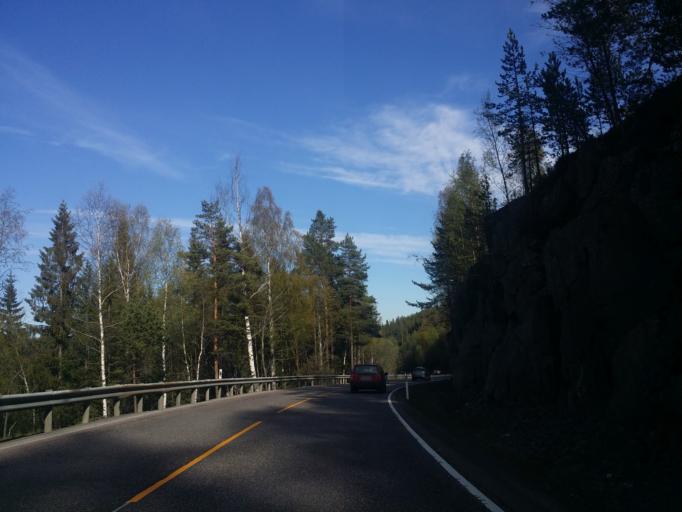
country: NO
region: Buskerud
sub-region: Kongsberg
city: Kongsberg
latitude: 59.6281
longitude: 9.5753
